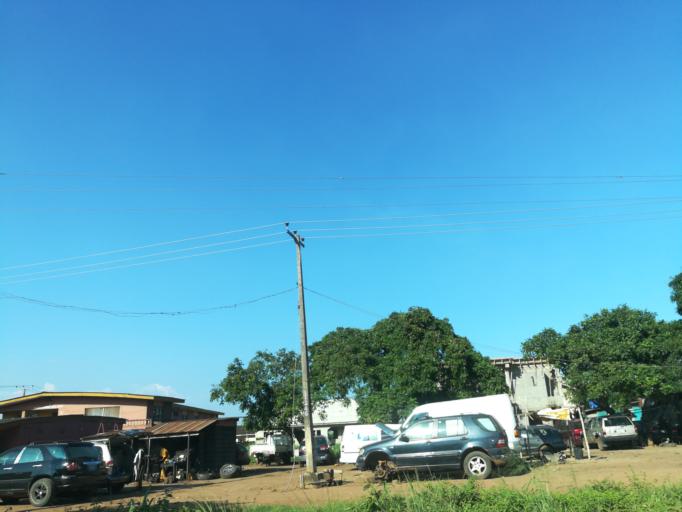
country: NG
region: Lagos
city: Ikorodu
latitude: 6.5761
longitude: 3.5273
